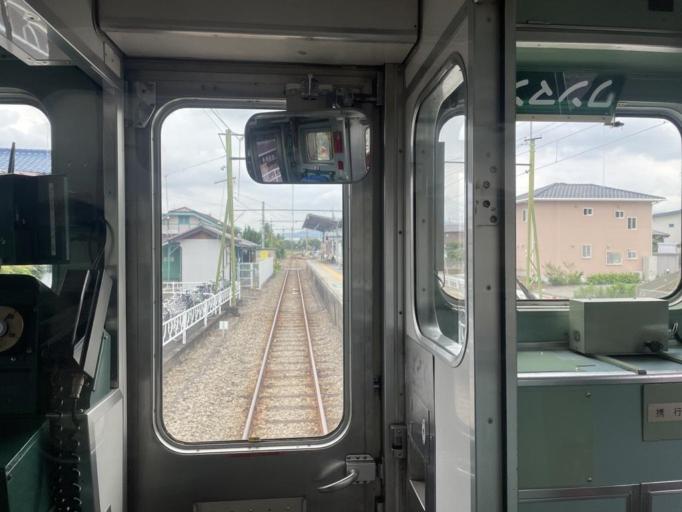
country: JP
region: Gunma
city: Fujioka
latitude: 36.2780
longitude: 139.0381
